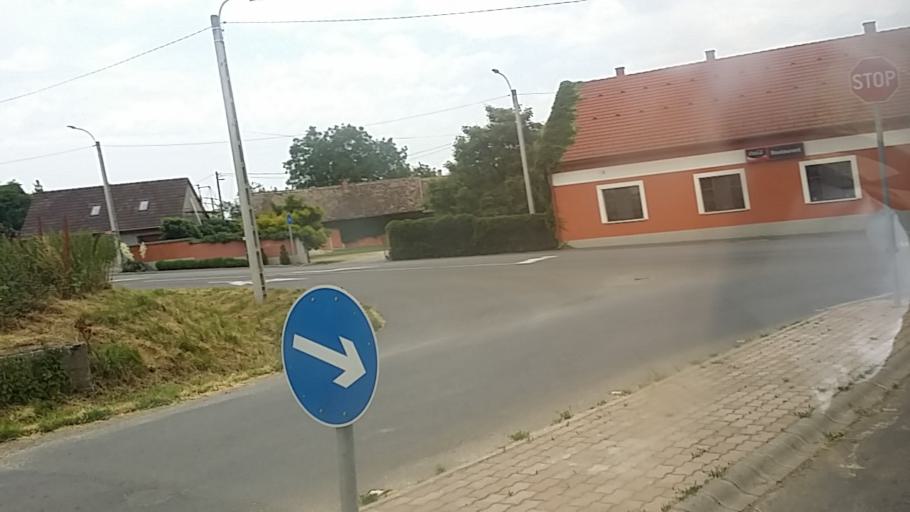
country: HU
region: Baranya
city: Boly
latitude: 45.9863
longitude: 18.5352
